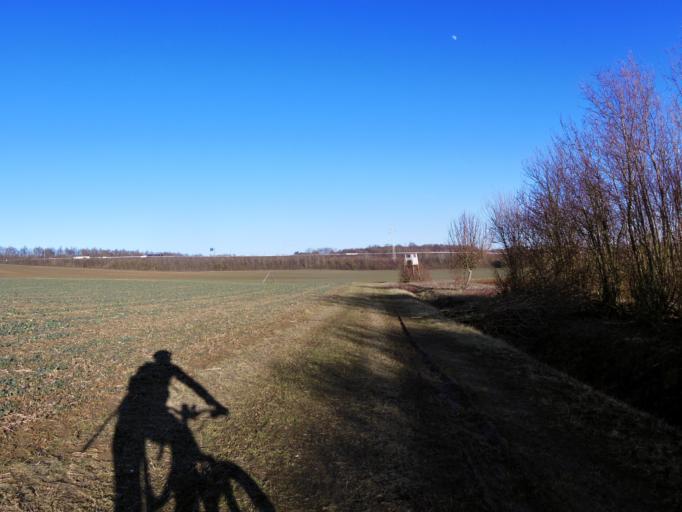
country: DE
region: Bavaria
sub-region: Regierungsbezirk Unterfranken
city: Estenfeld
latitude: 49.8457
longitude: 10.0015
